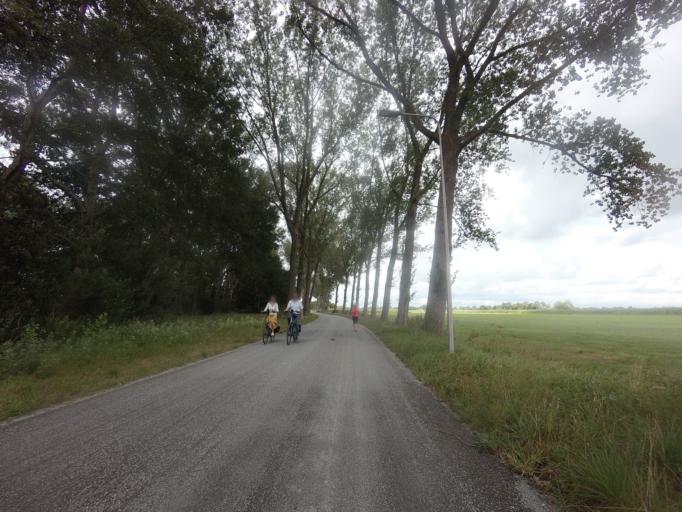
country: NL
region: Drenthe
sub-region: Gemeente Meppel
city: Meppel
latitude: 52.7115
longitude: 6.1772
